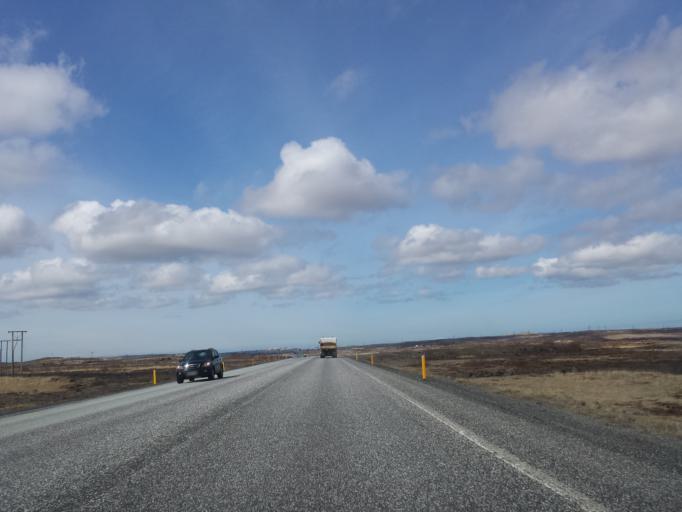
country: IS
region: Capital Region
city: Mosfellsbaer
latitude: 64.0746
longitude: -21.6429
